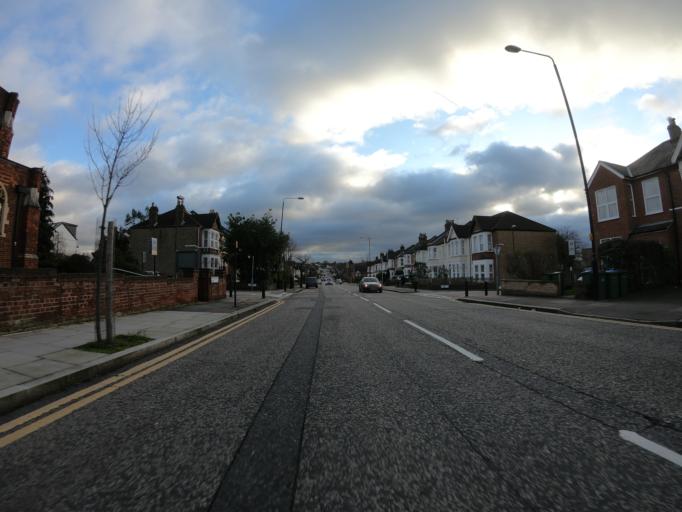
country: GB
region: England
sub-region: Greater London
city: Woolwich
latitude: 51.4606
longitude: 0.0581
